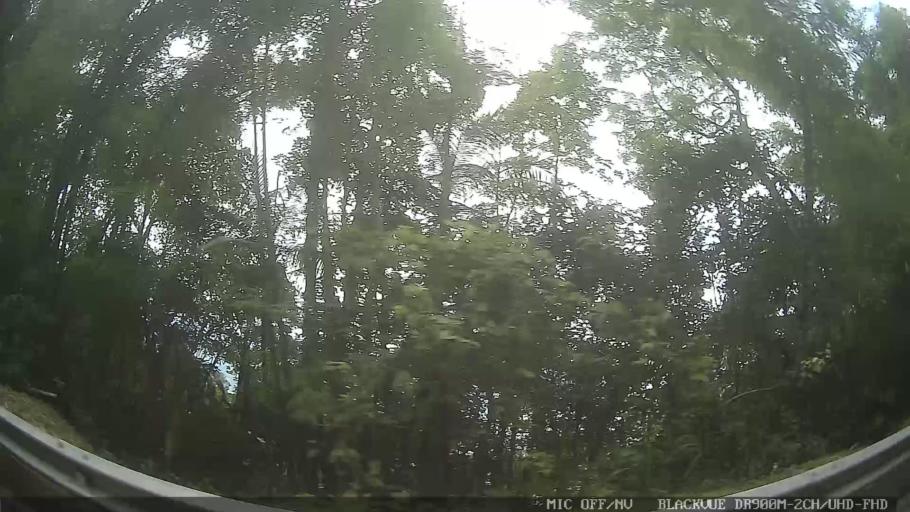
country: BR
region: Sao Paulo
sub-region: Caraguatatuba
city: Caraguatatuba
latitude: -23.5926
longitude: -45.4548
